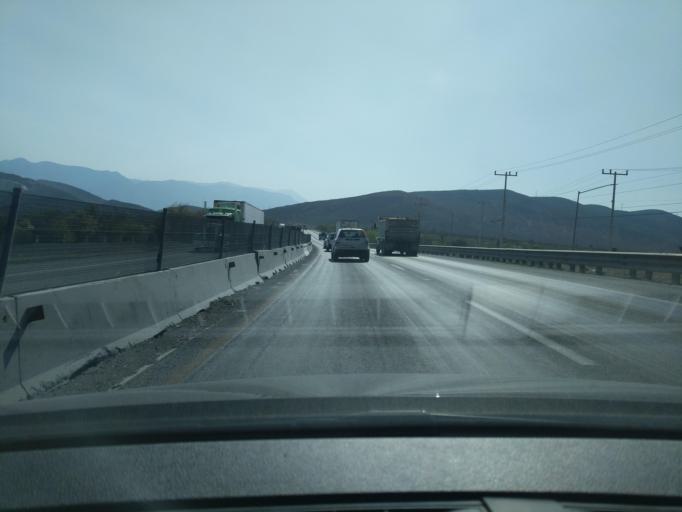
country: MX
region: Nuevo Leon
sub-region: Garcia
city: Los Parques
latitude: 25.7654
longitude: -100.4907
